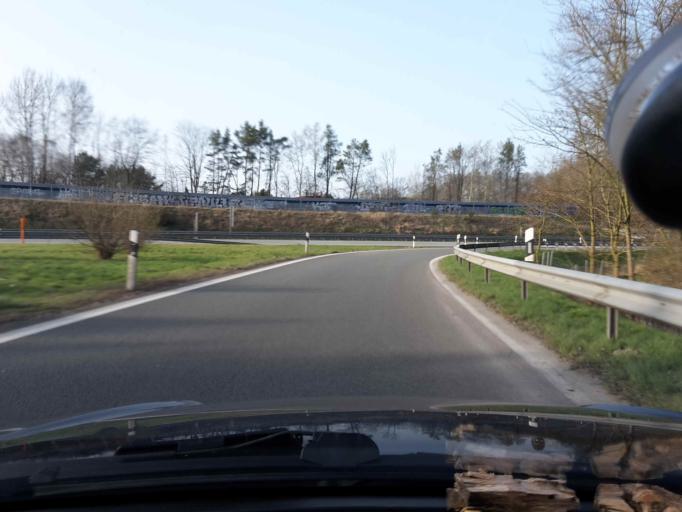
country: DE
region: Lower Saxony
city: Hollenstedt
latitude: 53.3586
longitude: 9.7138
